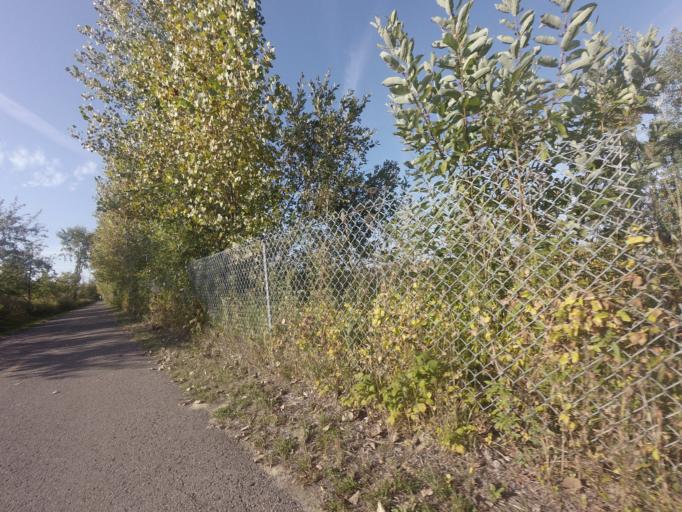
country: CA
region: Quebec
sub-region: Laurentides
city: Blainville
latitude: 45.7252
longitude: -73.9363
